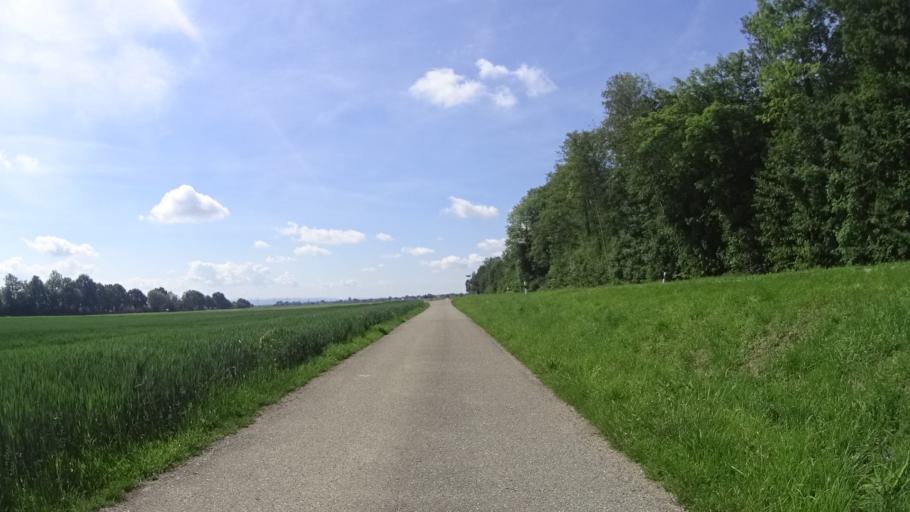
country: DE
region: Baden-Wuerttemberg
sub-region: Freiburg Region
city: Schutterwald
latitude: 48.4843
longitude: 7.8176
